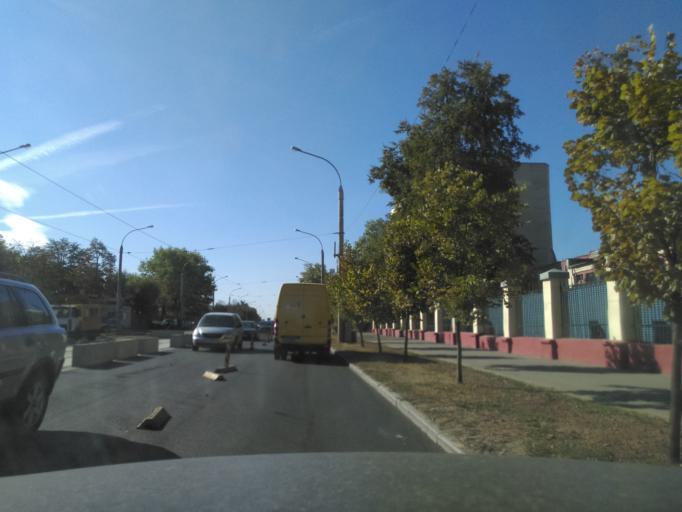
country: BY
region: Minsk
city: Minsk
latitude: 53.9046
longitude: 27.5963
